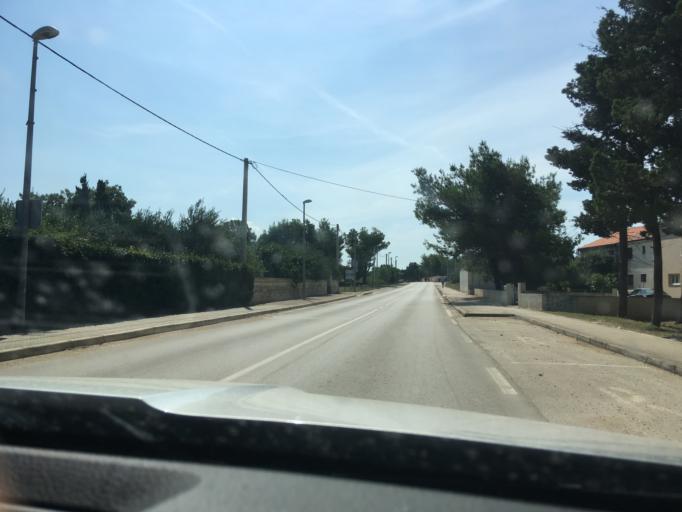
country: HR
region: Zadarska
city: Privlaka
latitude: 44.2588
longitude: 15.1232
